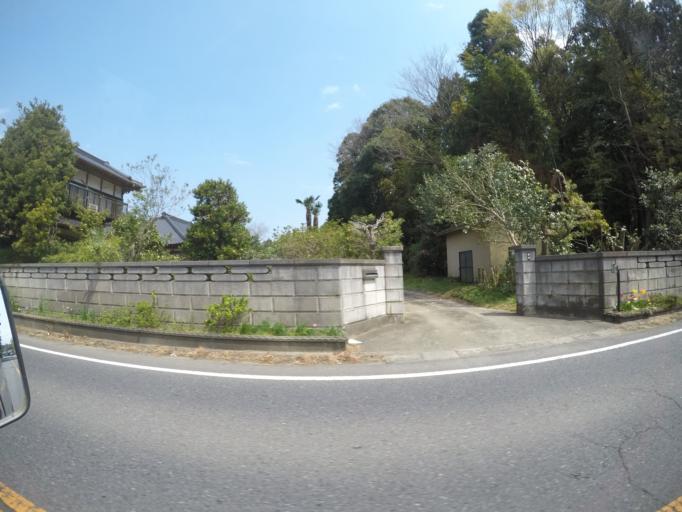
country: JP
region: Chiba
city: Sawara
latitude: 35.8675
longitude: 140.5411
